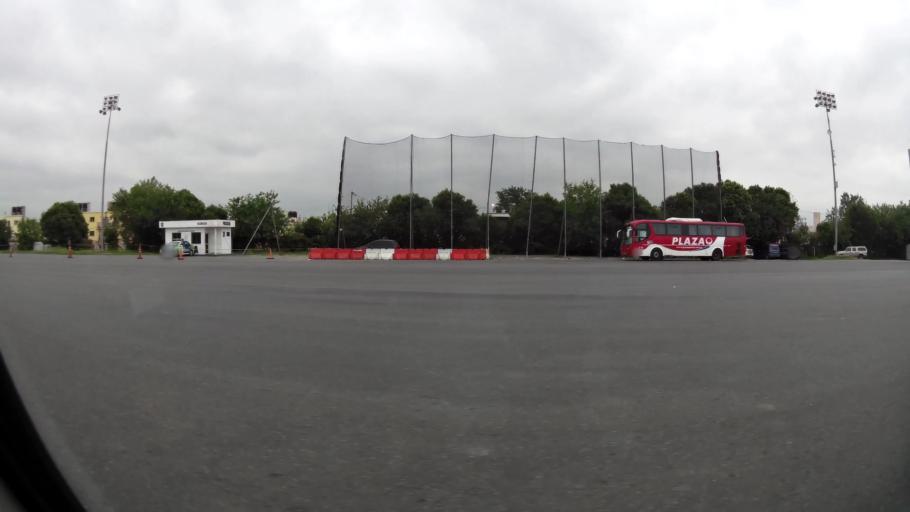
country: AR
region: Buenos Aires
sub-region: Partido de Avellaneda
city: Avellaneda
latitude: -34.6517
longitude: -58.3537
